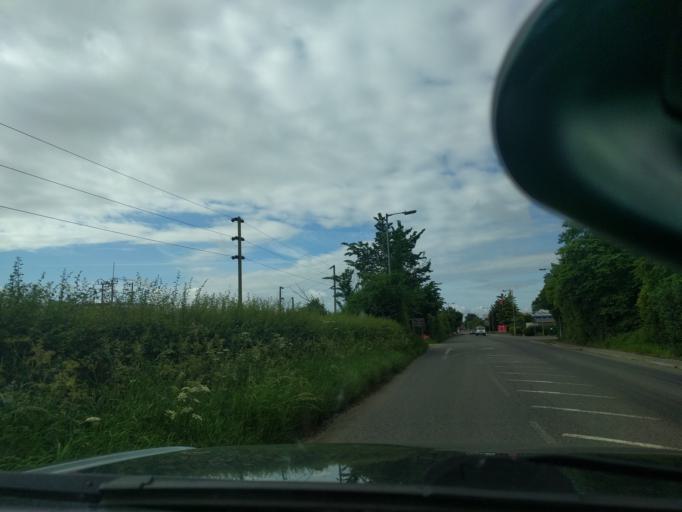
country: GB
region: England
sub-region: Wiltshire
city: Calne
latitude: 51.4518
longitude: -1.9939
